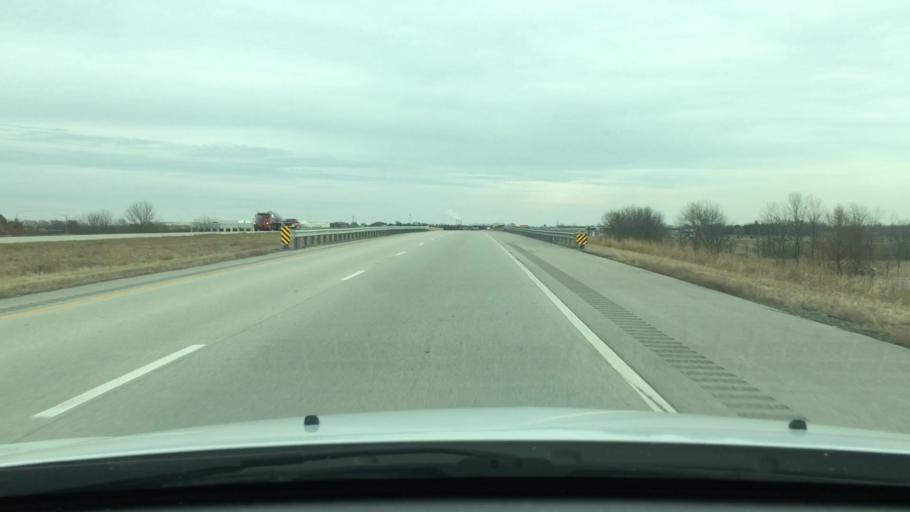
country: US
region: Illinois
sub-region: Sangamon County
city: Jerome
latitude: 39.7518
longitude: -89.7529
